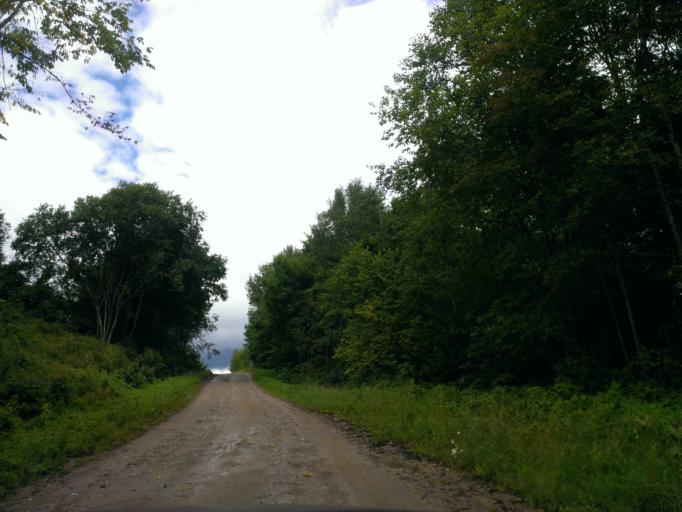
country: LV
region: Ligatne
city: Ligatne
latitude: 57.2150
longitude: 25.0111
